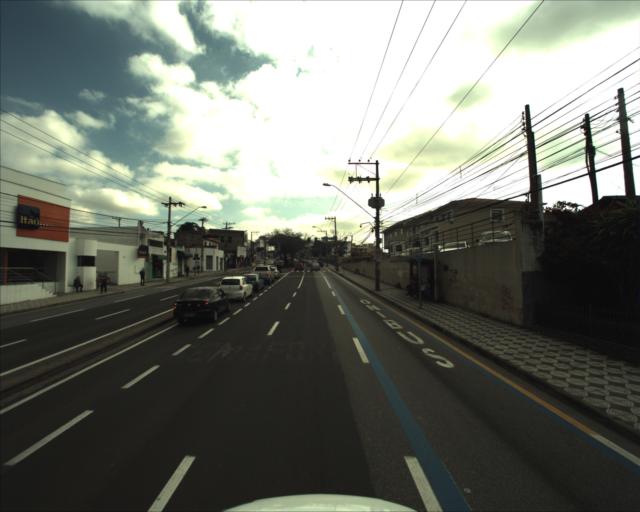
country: BR
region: Sao Paulo
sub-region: Sorocaba
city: Sorocaba
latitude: -23.5044
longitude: -47.4779
